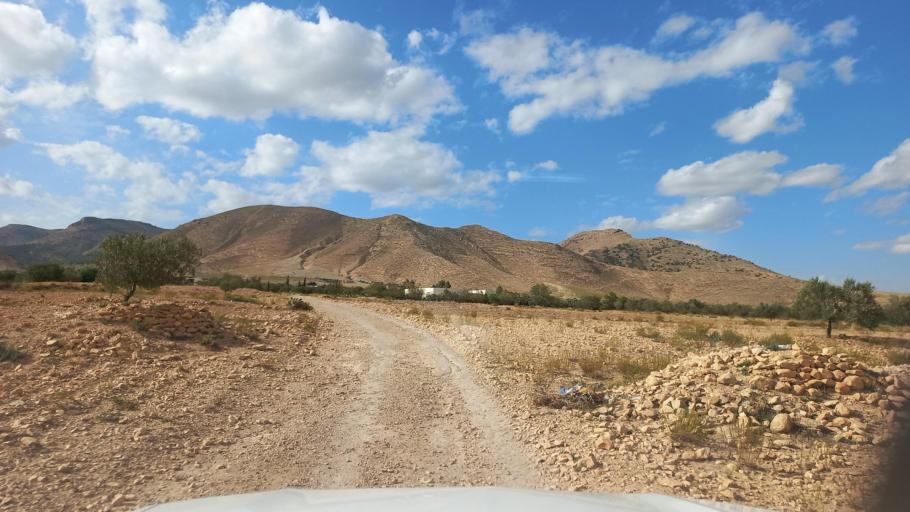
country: TN
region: Al Qasrayn
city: Sbiba
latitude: 35.4499
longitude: 9.0751
